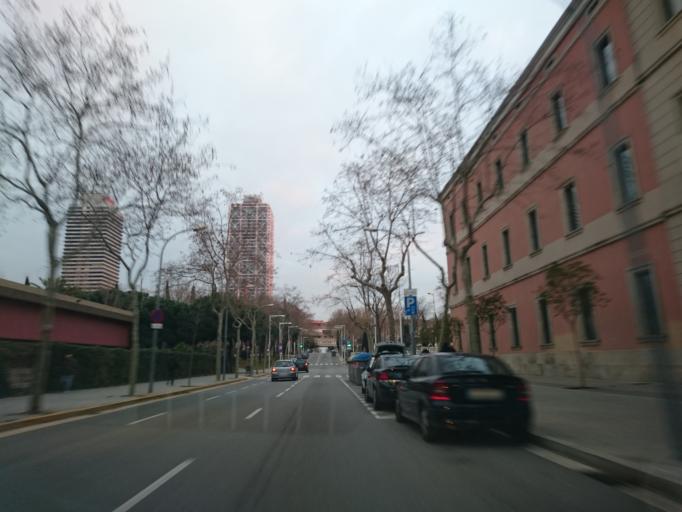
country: ES
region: Catalonia
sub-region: Provincia de Barcelona
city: Ciutat Vella
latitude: 41.3892
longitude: 2.1920
